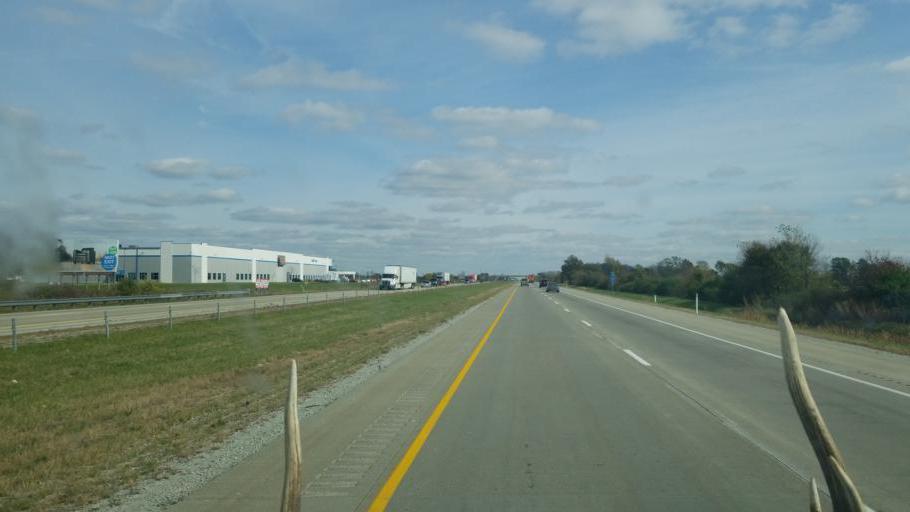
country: US
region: Indiana
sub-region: Marion County
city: Cumberland
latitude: 39.8195
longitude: -85.8889
